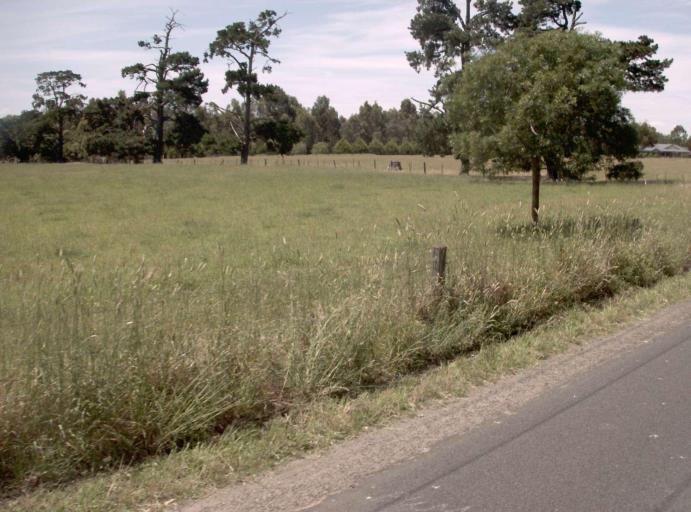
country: AU
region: Victoria
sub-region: Latrobe
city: Traralgon
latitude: -38.1793
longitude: 146.6272
